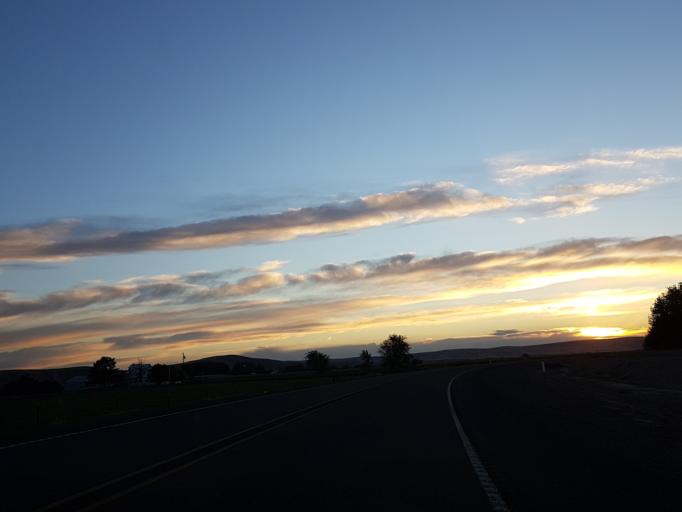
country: US
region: Oregon
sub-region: Malheur County
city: Vale
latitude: 43.9364
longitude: -117.3134
